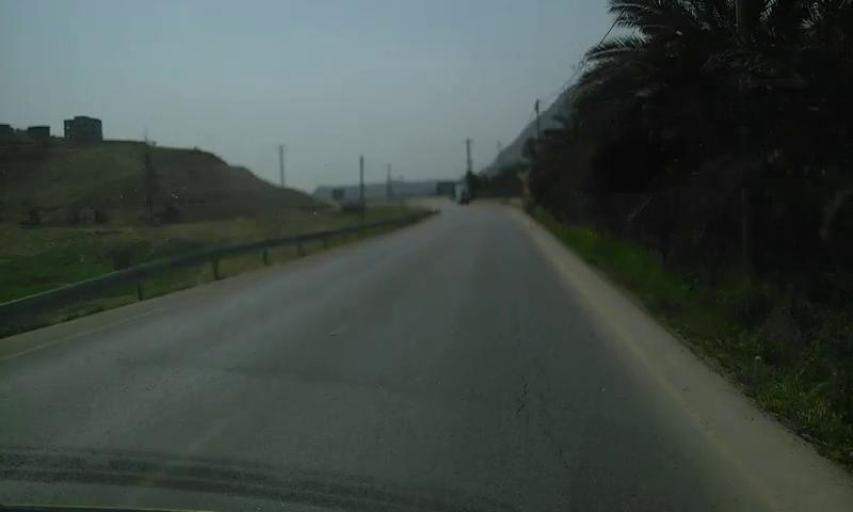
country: PS
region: West Bank
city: An Nuway`imah
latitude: 31.8933
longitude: 35.4294
